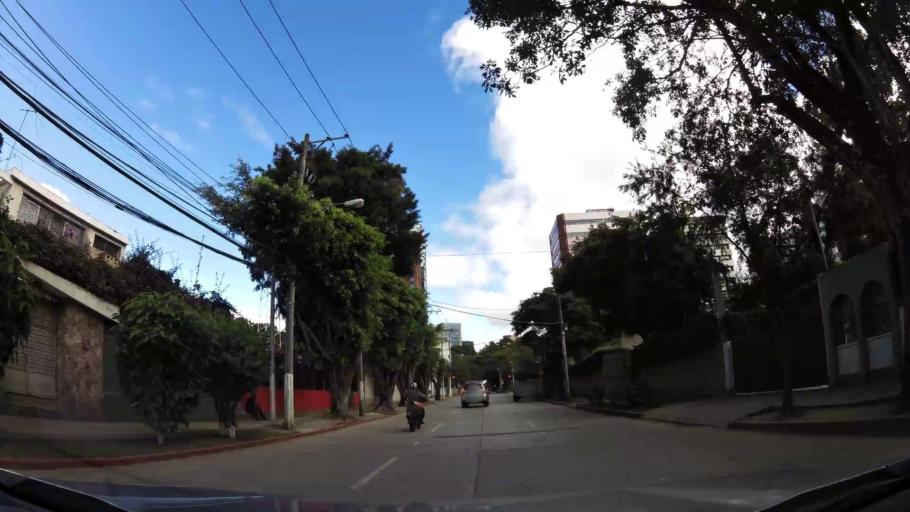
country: GT
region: Guatemala
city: Santa Catarina Pinula
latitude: 14.5943
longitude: -90.5137
